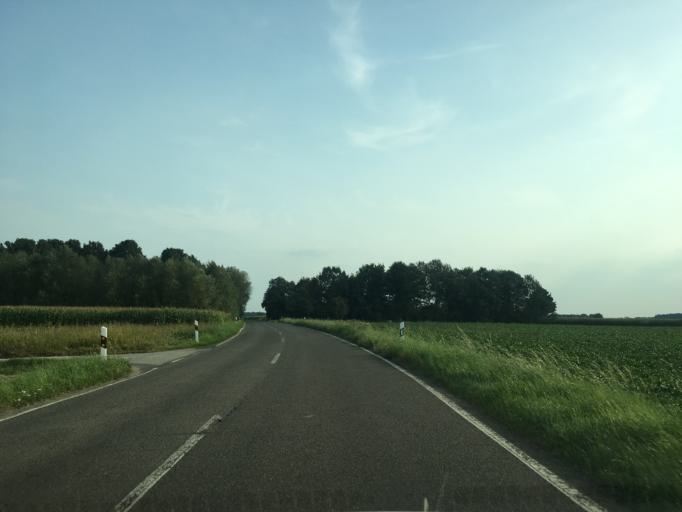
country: DE
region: North Rhine-Westphalia
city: Huckelhoven
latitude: 51.0906
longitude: 6.2221
